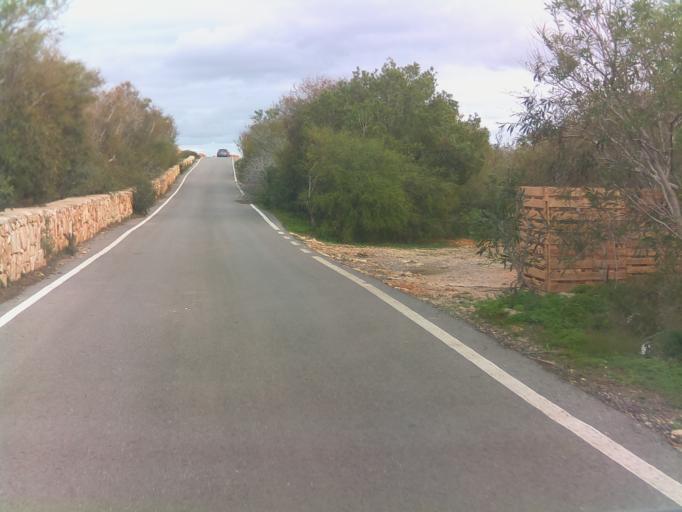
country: MT
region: Il-Mellieha
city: Mellieha
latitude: 35.9876
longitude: 14.3735
